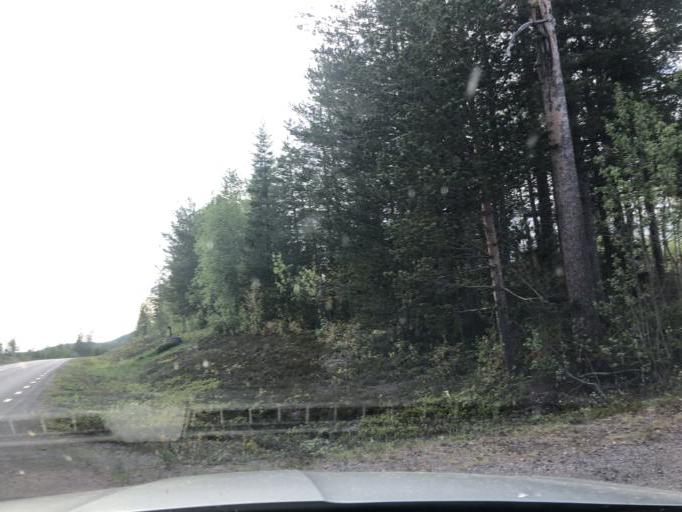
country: SE
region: Norrbotten
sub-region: Arvidsjaurs Kommun
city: Arvidsjaur
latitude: 65.6082
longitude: 19.0852
